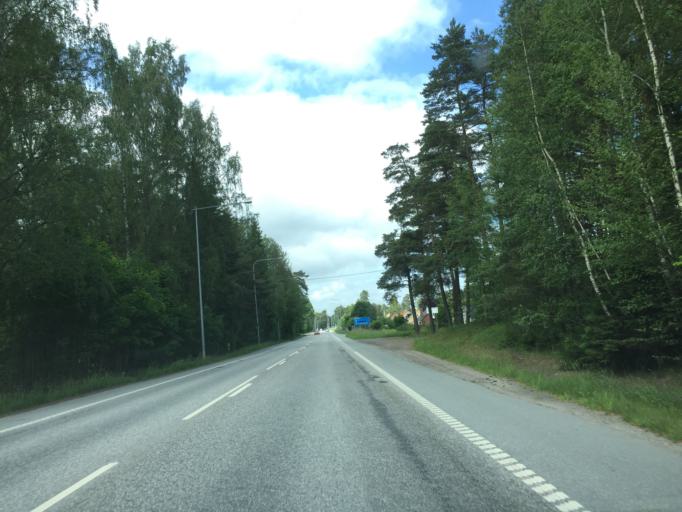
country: SE
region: OErebro
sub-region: Orebro Kommun
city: Orebro
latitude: 59.2209
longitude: 15.1454
